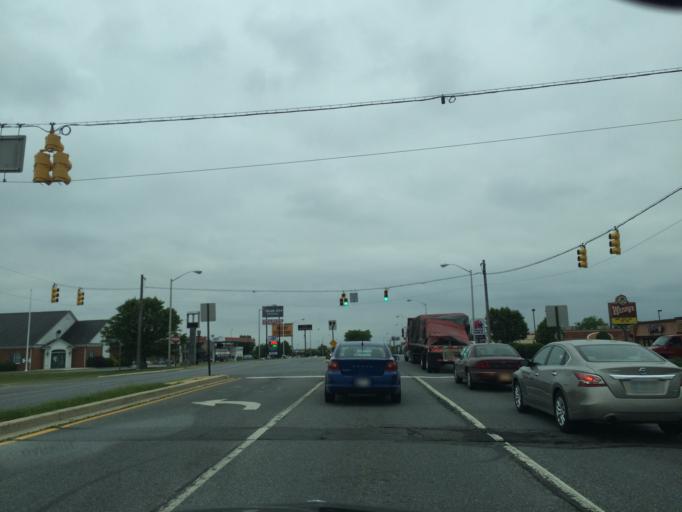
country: US
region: Maryland
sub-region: Washington County
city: Halfway
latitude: 39.6324
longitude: -77.7597
